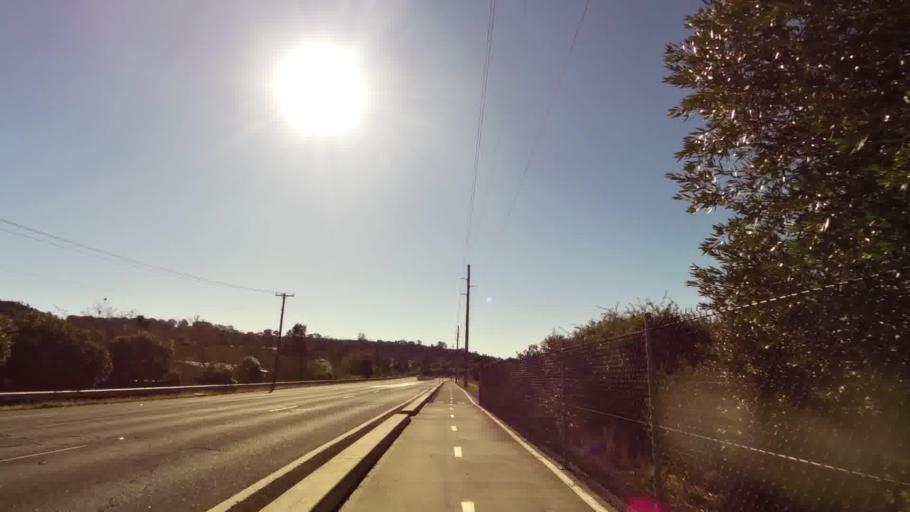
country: AU
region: New South Wales
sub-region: Wollongong
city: Koonawarra
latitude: -34.4727
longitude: 150.8154
